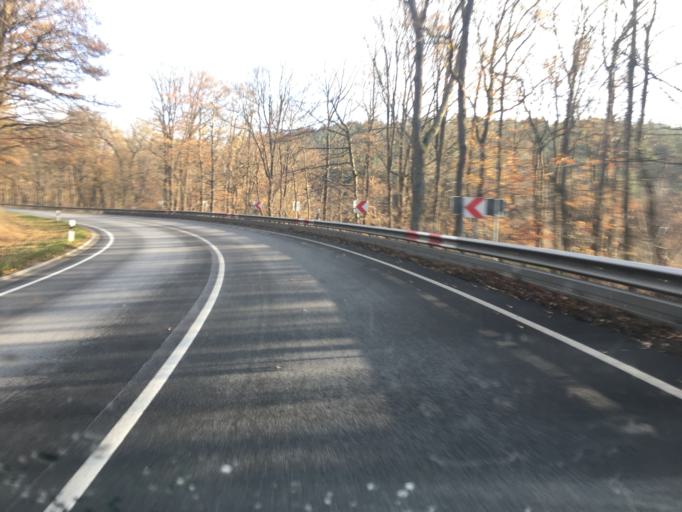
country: DE
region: North Rhine-Westphalia
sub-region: Regierungsbezirk Koln
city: Kall
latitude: 50.5548
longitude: 6.5428
